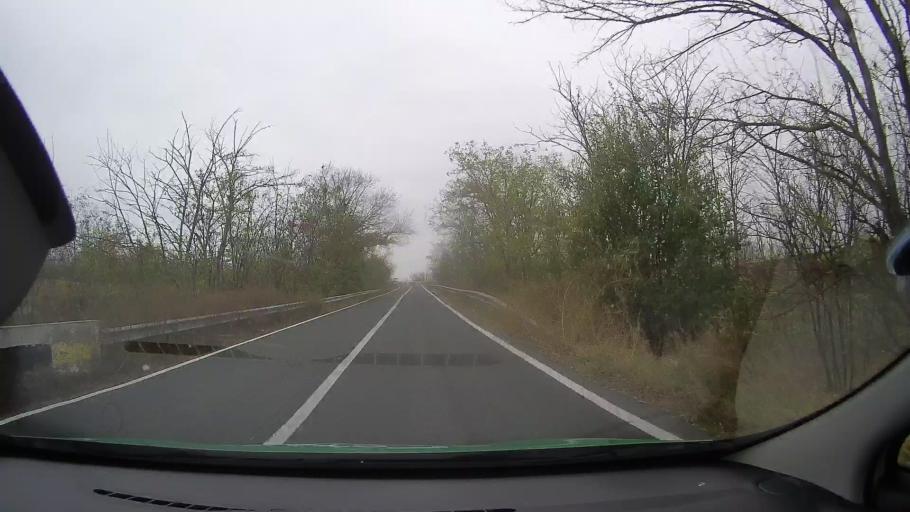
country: RO
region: Constanta
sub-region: Comuna Saraiu
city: Saraiu
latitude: 44.7128
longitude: 28.1264
